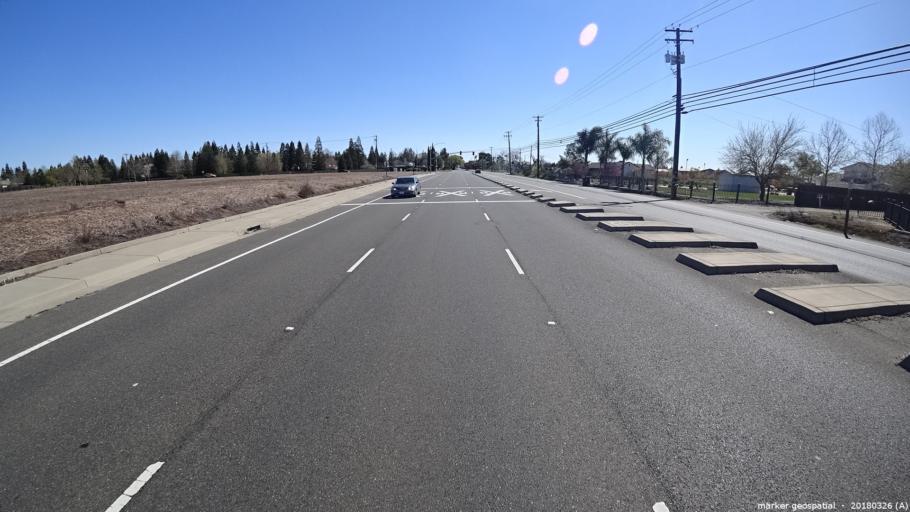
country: US
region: California
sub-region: Sacramento County
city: Vineyard
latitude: 38.4527
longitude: -121.3178
